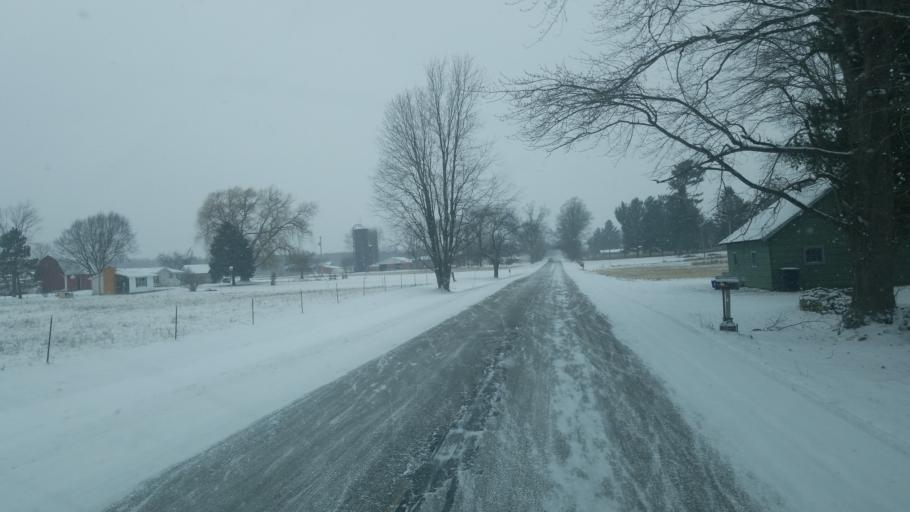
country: US
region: Michigan
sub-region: Mecosta County
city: Big Rapids
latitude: 43.7480
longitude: -85.4032
